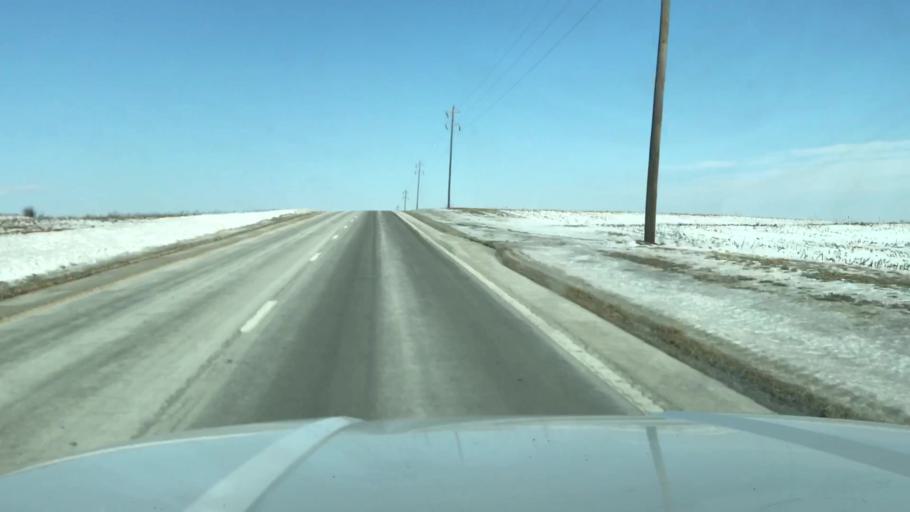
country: US
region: Missouri
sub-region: Andrew County
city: Savannah
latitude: 40.1210
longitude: -94.8697
